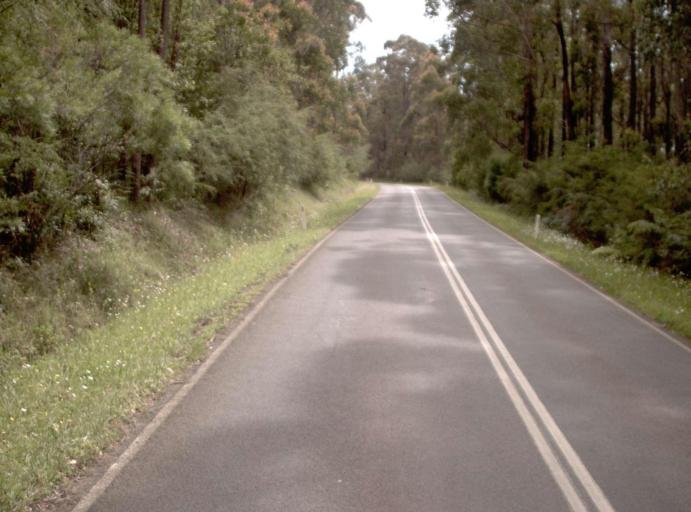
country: AU
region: Victoria
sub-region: Latrobe
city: Traralgon
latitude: -38.0185
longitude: 146.4194
